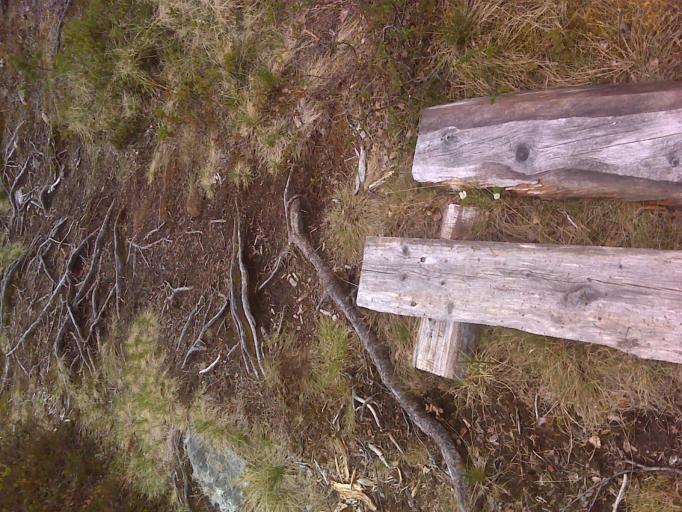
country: NO
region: Troms
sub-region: Berg
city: Skaland
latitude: 69.2022
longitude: 17.4065
